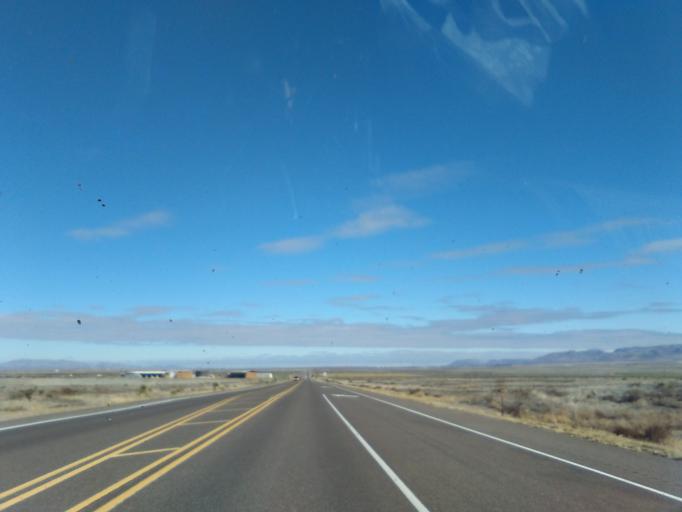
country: US
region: New Mexico
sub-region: Dona Ana County
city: Hatch
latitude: 32.5808
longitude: -107.3833
